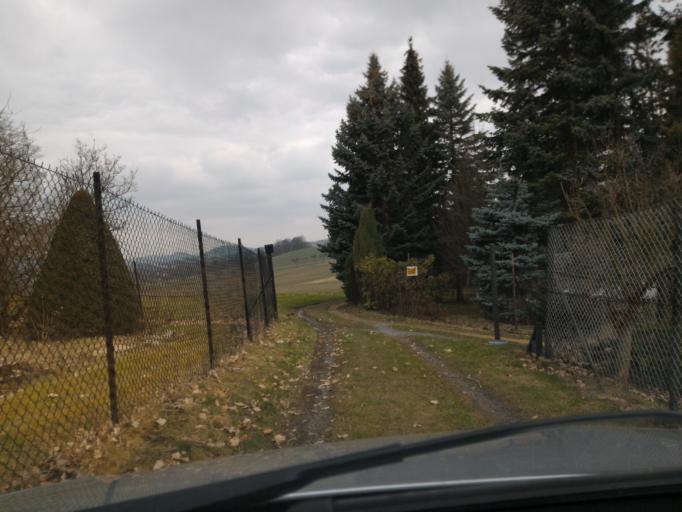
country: DE
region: Saxony
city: Grossschonau
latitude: 50.9033
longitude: 14.6669
